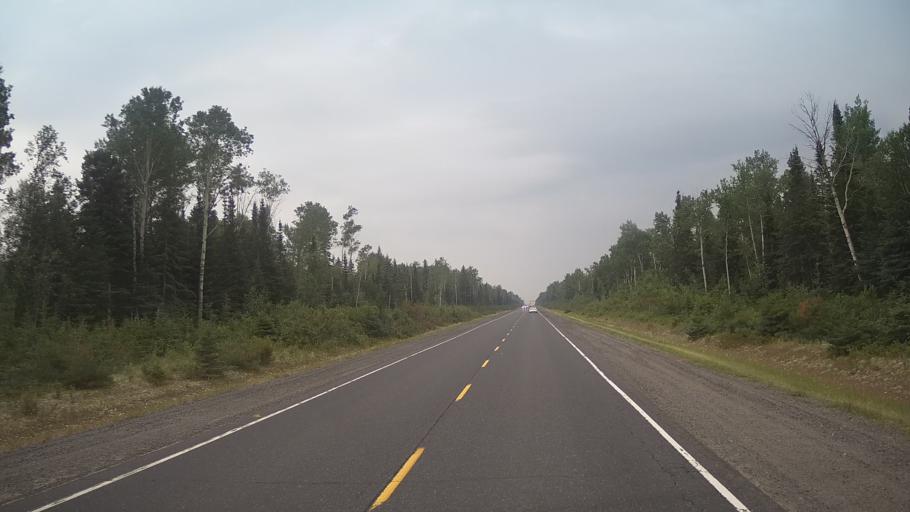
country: CA
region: Ontario
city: Greenstone
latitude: 49.2289
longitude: -88.1875
